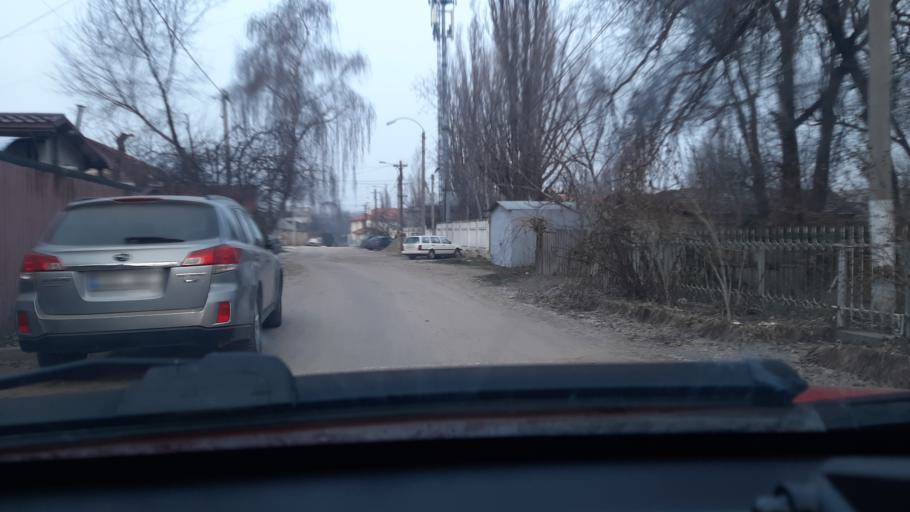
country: MD
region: Chisinau
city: Chisinau
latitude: 46.9878
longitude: 28.8921
